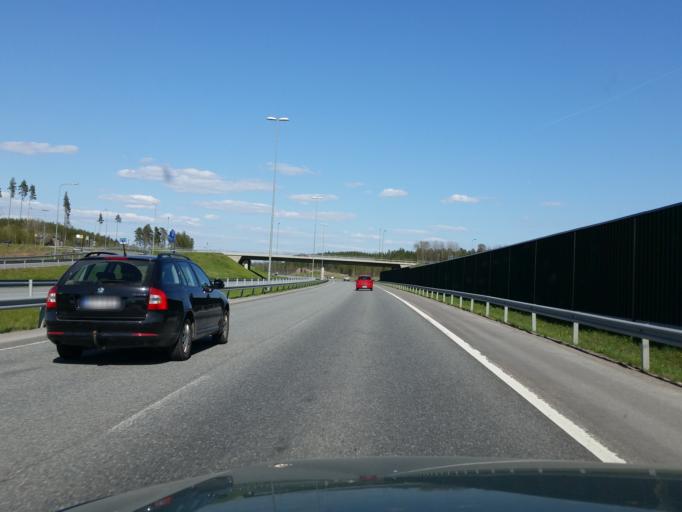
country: FI
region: Uusimaa
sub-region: Helsinki
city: Kirkkonummi
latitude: 60.1179
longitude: 24.4756
